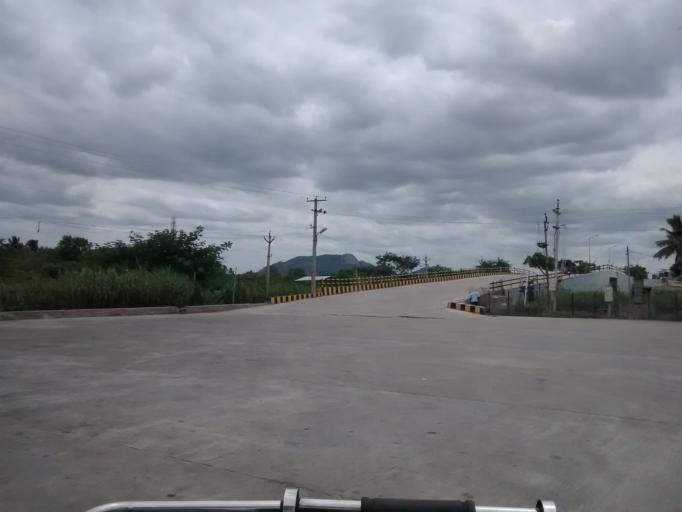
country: IN
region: Andhra Pradesh
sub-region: Chittoor
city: Chittoor
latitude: 13.2753
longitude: 79.0352
